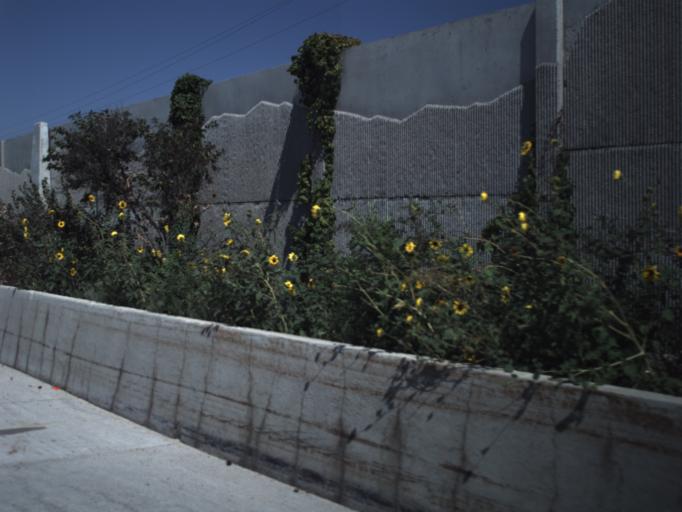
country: US
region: Utah
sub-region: Salt Lake County
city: Midvale
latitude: 40.6135
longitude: -111.9058
